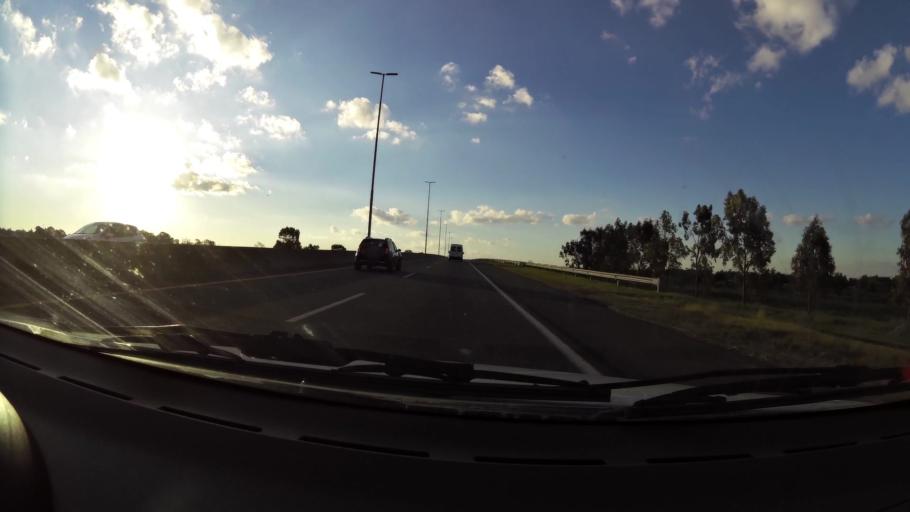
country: AR
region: Buenos Aires
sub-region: Partido de La Plata
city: La Plata
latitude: -34.8617
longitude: -58.0183
